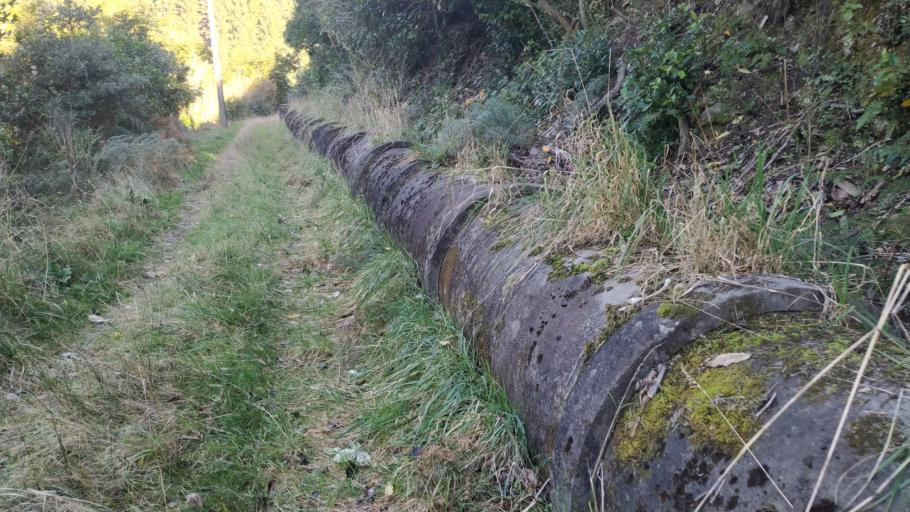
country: NZ
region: Nelson
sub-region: Nelson City
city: Nelson
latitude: -41.2971
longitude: 173.3398
